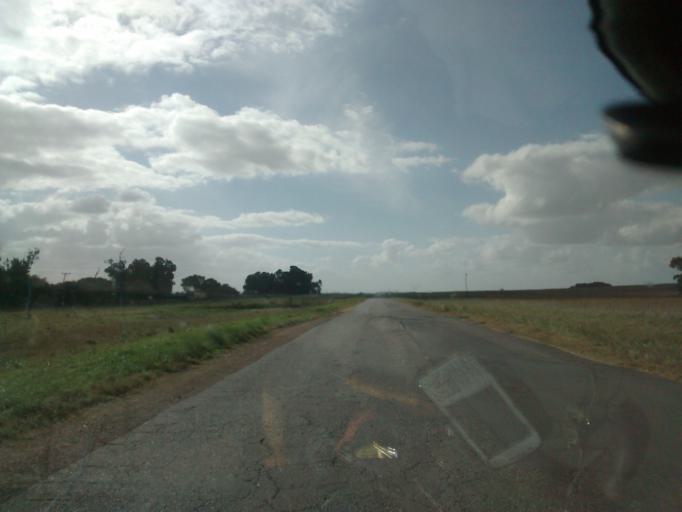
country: AR
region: Buenos Aires
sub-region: Partido de Tandil
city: Tandil
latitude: -37.6136
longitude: -58.7473
